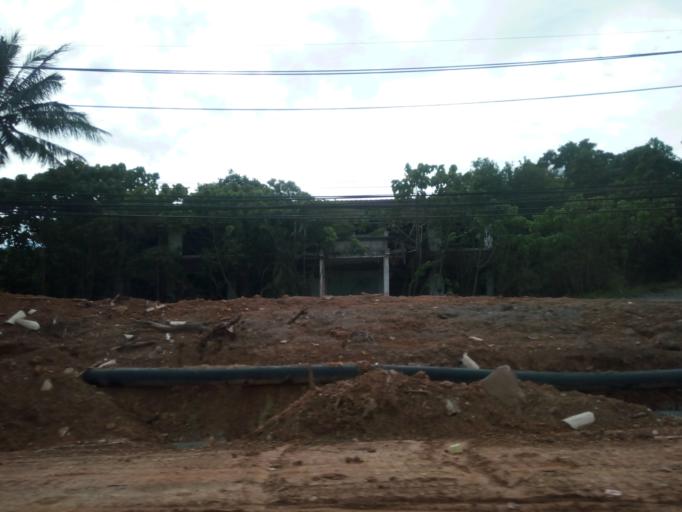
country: TH
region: Phuket
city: Mueang Phuket
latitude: 7.8359
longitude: 98.3941
